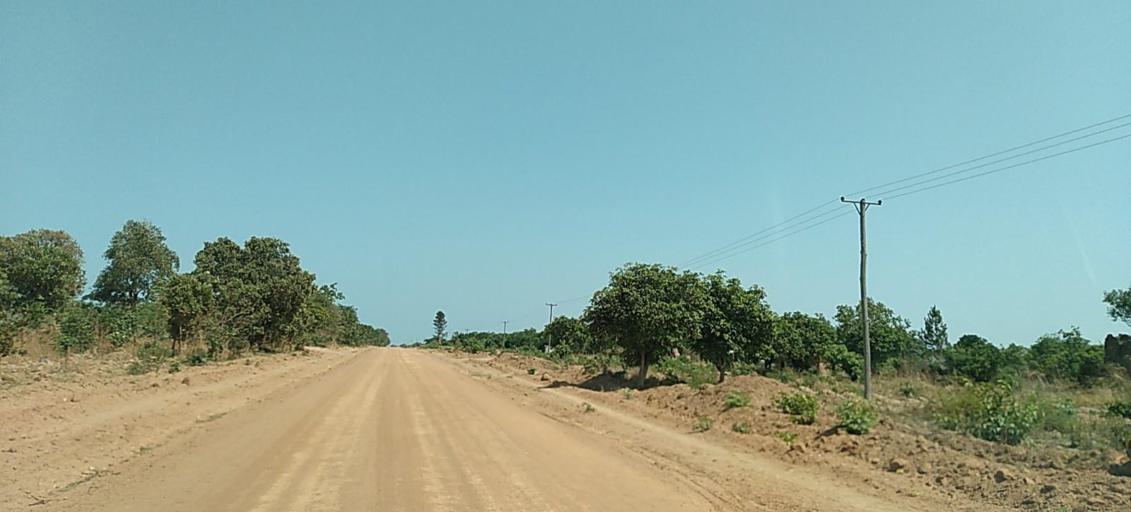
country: ZM
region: Copperbelt
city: Luanshya
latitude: -13.4783
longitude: 28.6805
